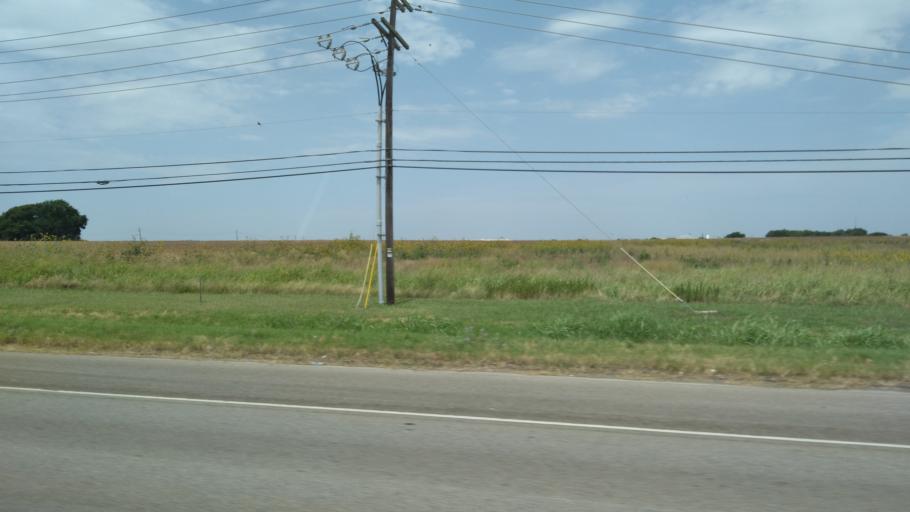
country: US
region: Texas
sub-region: McLennan County
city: Beverly Hills
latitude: 31.4940
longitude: -97.1663
